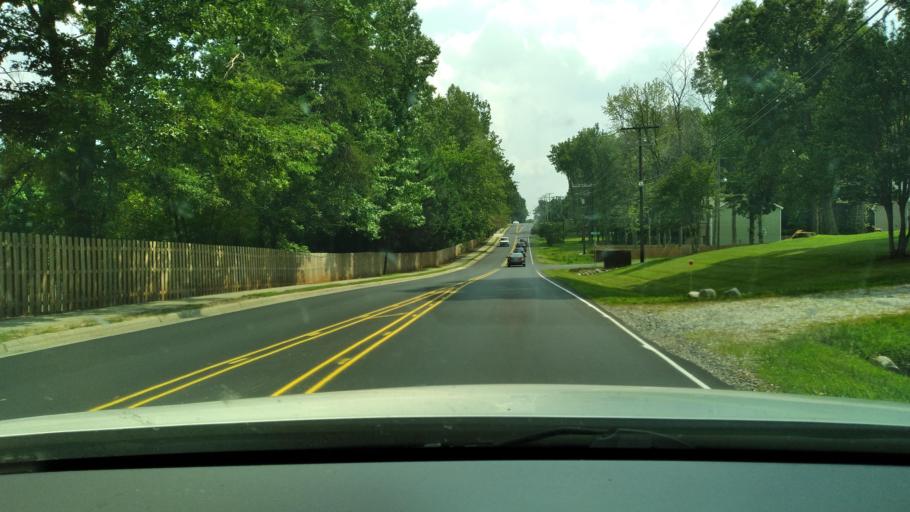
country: US
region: North Carolina
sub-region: Guilford County
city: Jamestown
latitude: 36.0491
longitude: -79.8903
